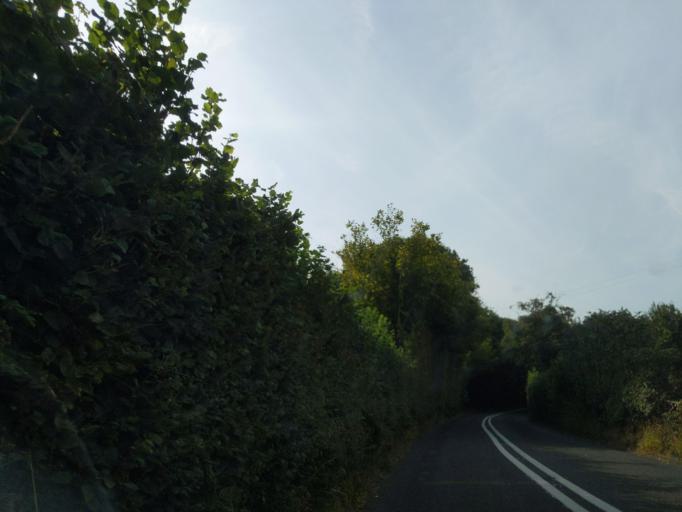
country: GB
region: England
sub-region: Devon
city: Winkleigh
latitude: 50.9438
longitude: -3.9203
